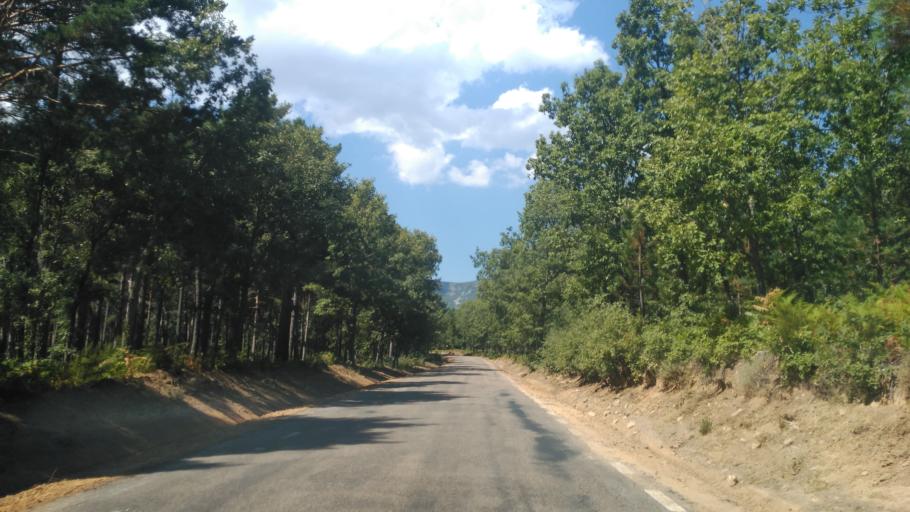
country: ES
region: Castille and Leon
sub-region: Provincia de Salamanca
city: Nava de Francia
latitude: 40.5249
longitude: -6.1316
